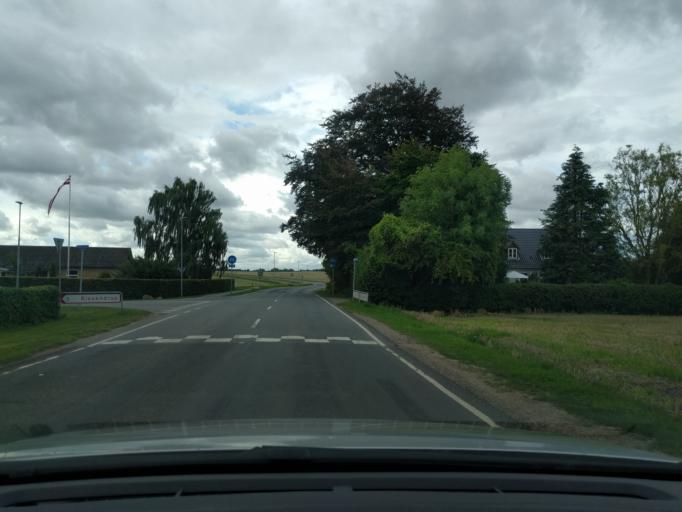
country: DK
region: South Denmark
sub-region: Nyborg Kommune
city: Ullerslev
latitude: 55.3813
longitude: 10.6668
